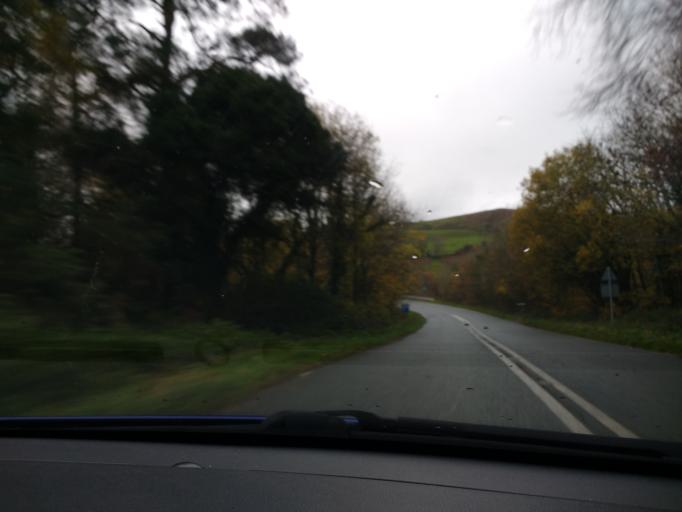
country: GB
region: England
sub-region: Cumbria
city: Millom
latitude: 54.2714
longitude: -3.2446
